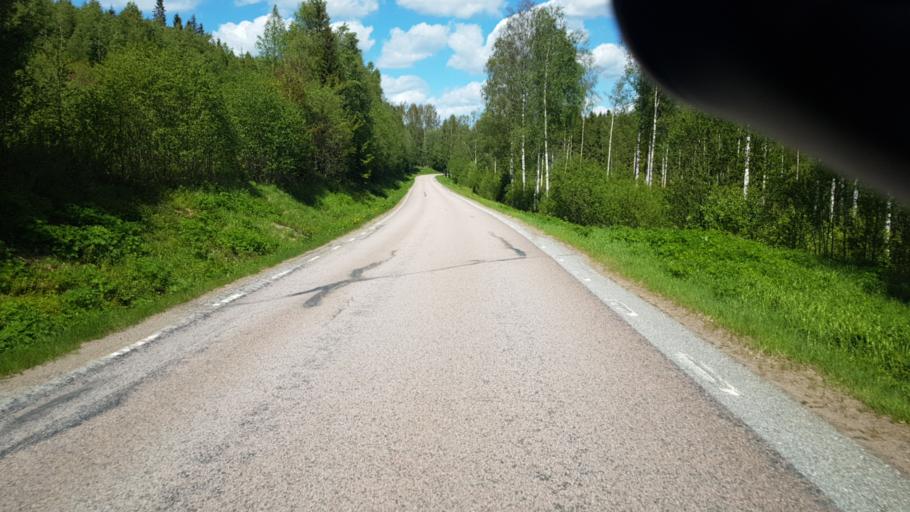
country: SE
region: Vaermland
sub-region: Arvika Kommun
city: Arvika
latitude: 59.7138
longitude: 12.7960
